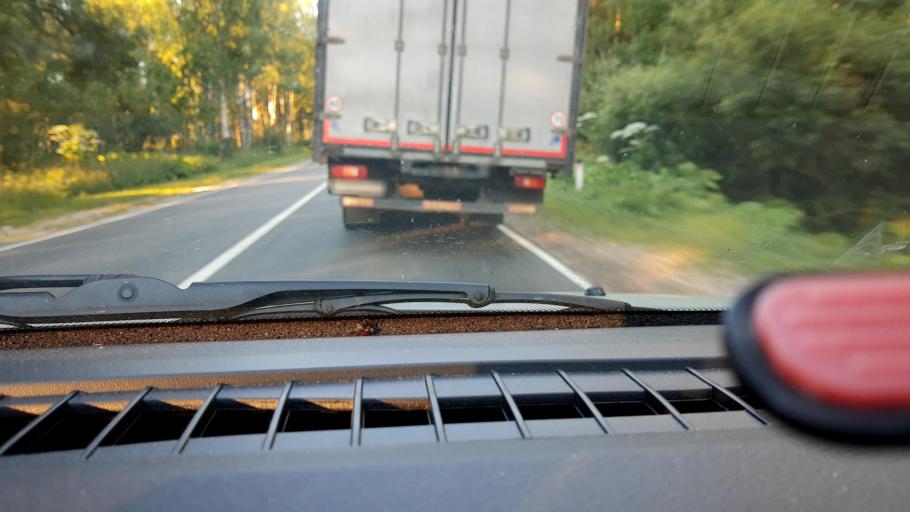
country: RU
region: Nizjnij Novgorod
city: Sukhobezvodnoye
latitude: 56.8642
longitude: 44.9105
